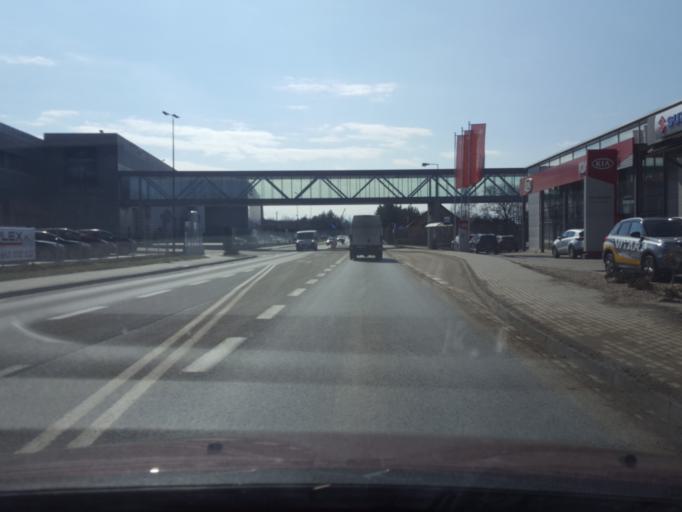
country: PL
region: Lesser Poland Voivodeship
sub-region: Powiat nowosadecki
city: Chelmiec
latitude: 49.6702
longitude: 20.6864
